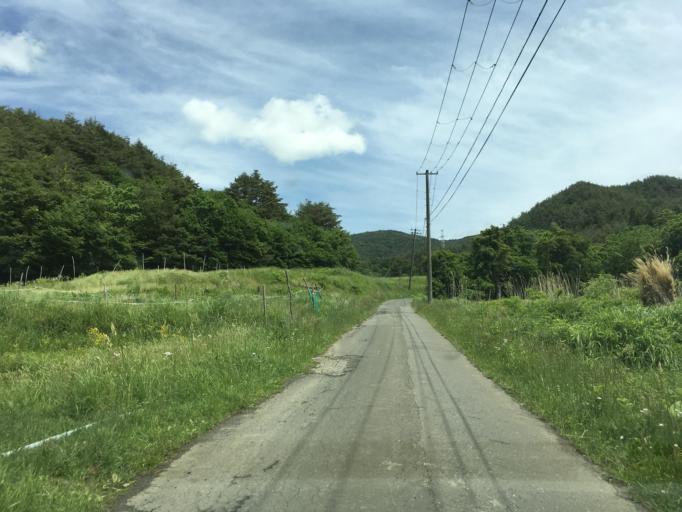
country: JP
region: Iwate
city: Mizusawa
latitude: 39.1273
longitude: 141.2757
